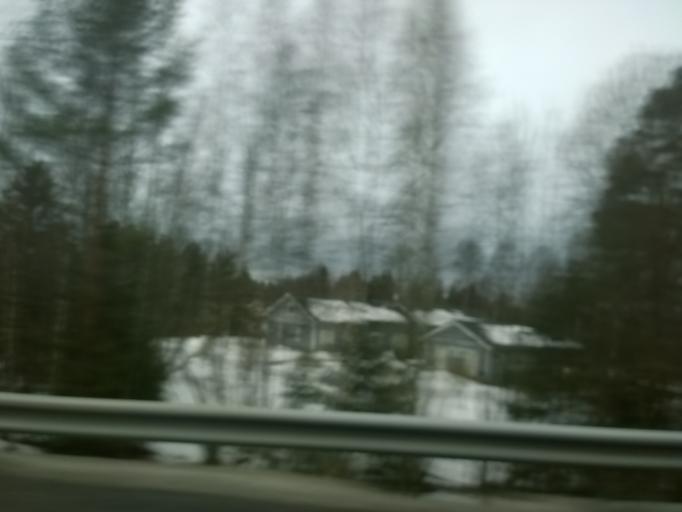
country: FI
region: Pirkanmaa
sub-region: Tampere
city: Lempaeaelae
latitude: 61.3582
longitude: 23.7887
